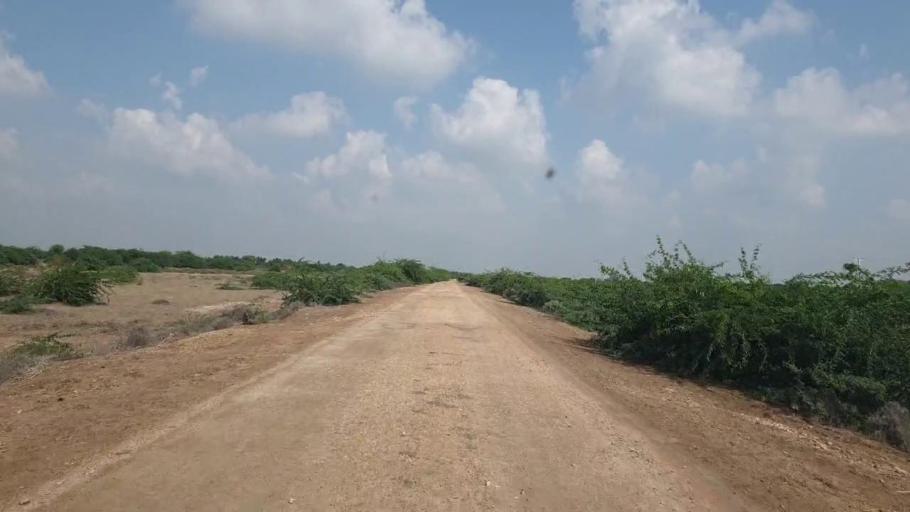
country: PK
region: Sindh
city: Badin
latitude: 24.4879
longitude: 68.6506
